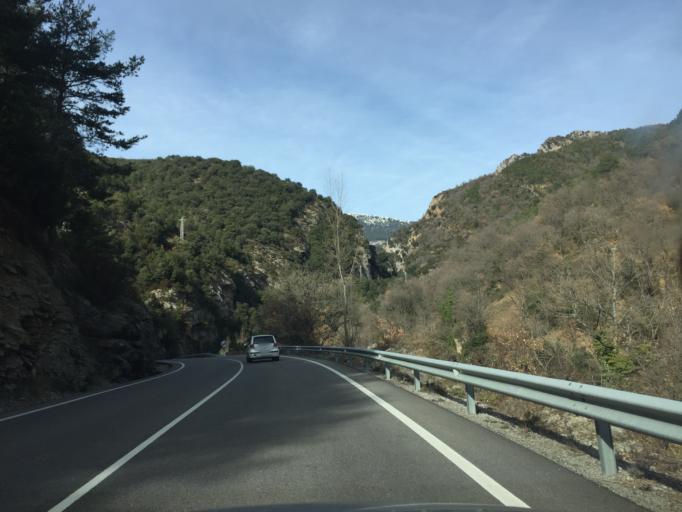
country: ES
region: Aragon
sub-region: Provincia de Huesca
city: Laspuna
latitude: 42.5516
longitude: 0.2025
